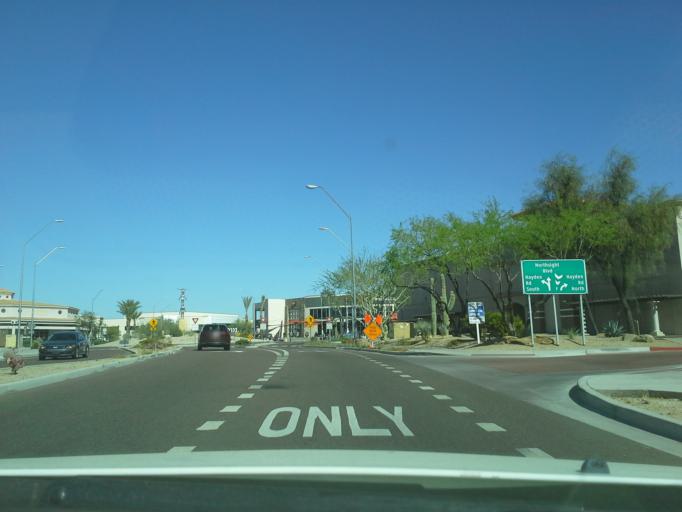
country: US
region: Arizona
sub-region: Maricopa County
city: Paradise Valley
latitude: 33.6265
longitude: -111.8950
